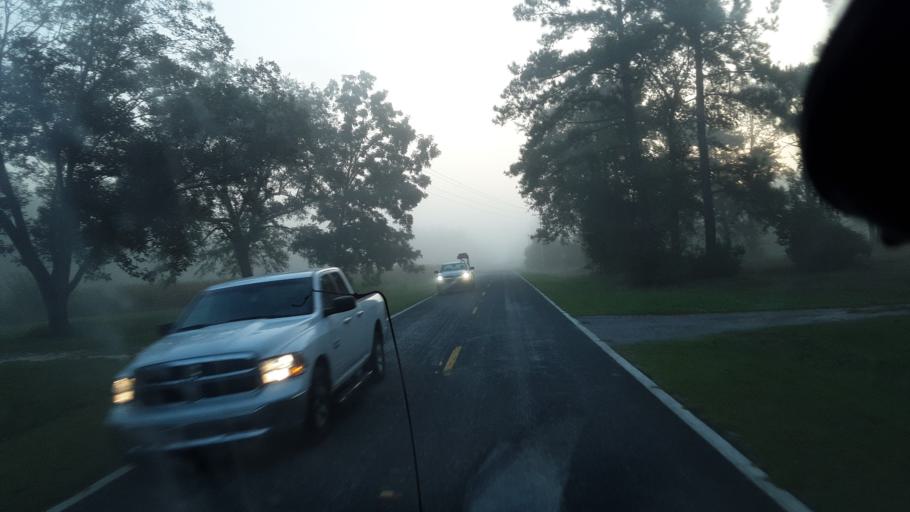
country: US
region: South Carolina
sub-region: Clarendon County
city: Manning
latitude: 33.7218
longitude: -80.1260
